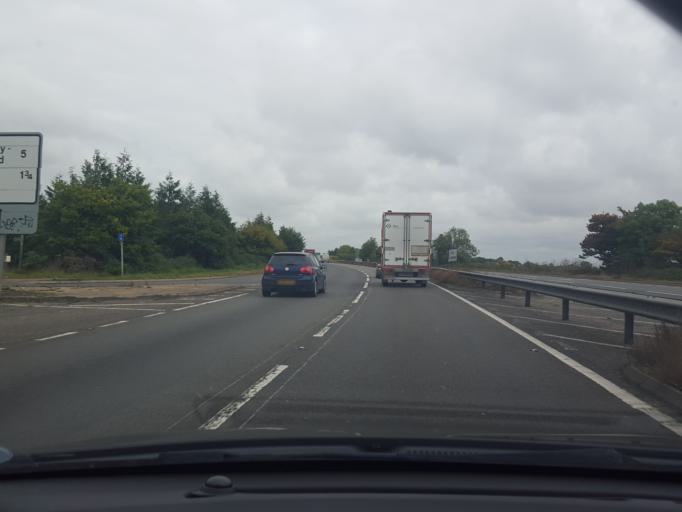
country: GB
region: England
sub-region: Suffolk
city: East Bergholt
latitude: 51.9824
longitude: 1.0000
